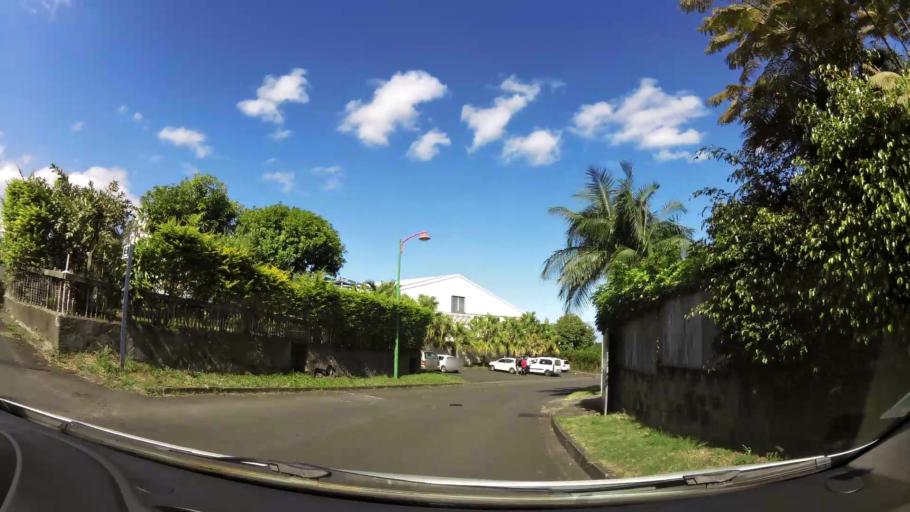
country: RE
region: Reunion
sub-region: Reunion
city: Le Tampon
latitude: -21.2791
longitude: 55.5038
